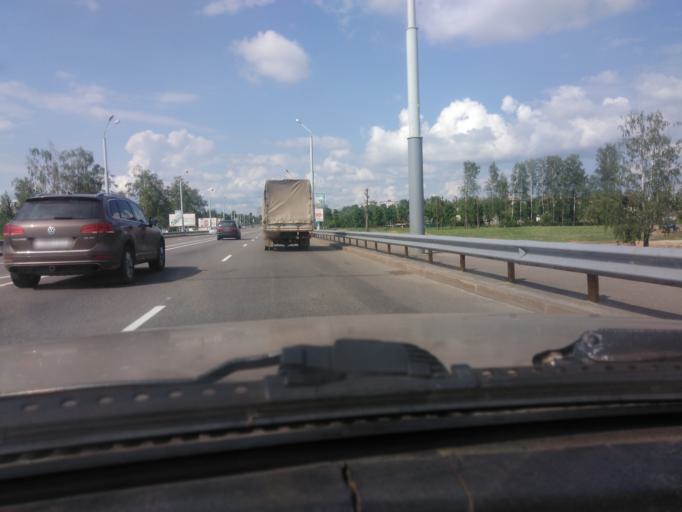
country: BY
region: Mogilev
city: Mahilyow
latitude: 53.9235
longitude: 30.3498
